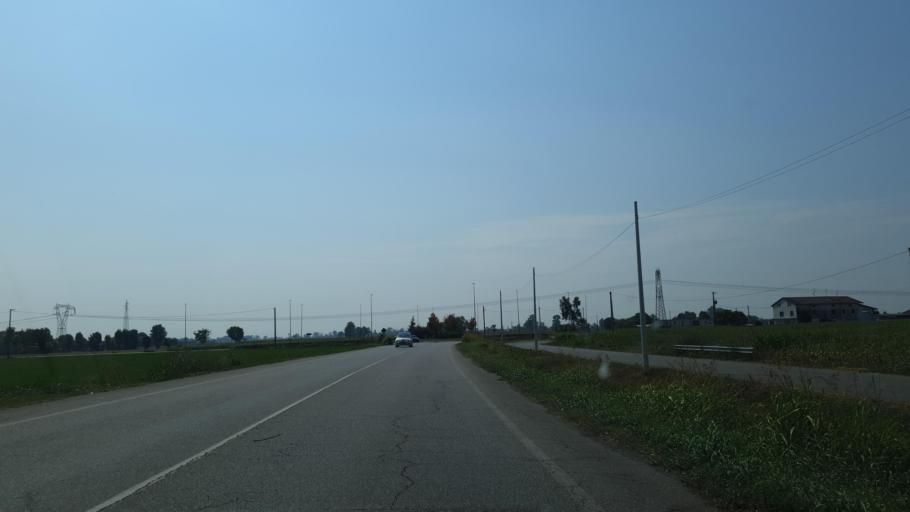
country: IT
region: Lombardy
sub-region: Provincia di Brescia
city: Ghedi
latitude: 45.4026
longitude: 10.2529
